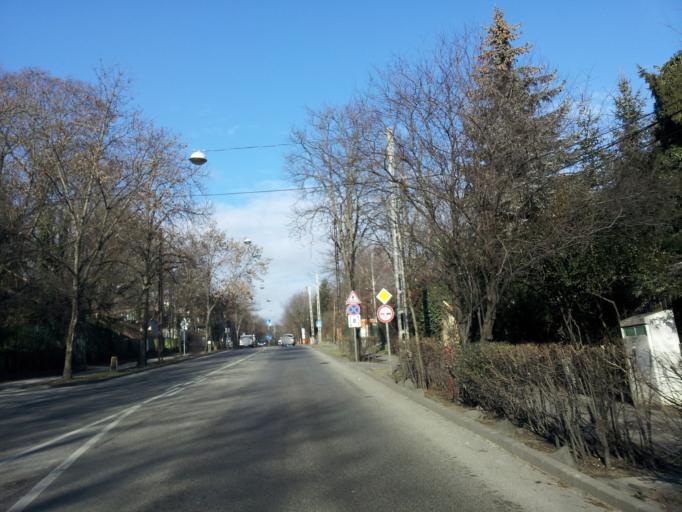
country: HU
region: Budapest
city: Budapest XII. keruelet
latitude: 47.5250
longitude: 18.9856
